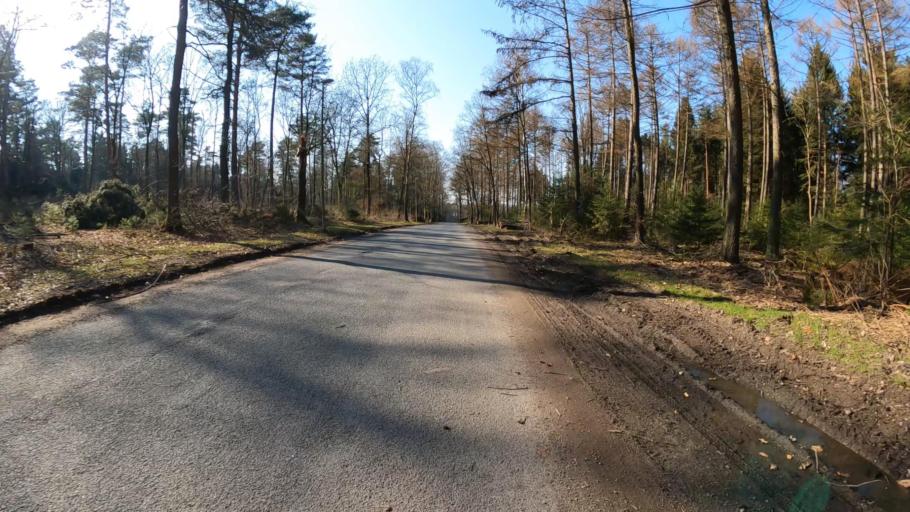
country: DE
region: Lower Saxony
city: Buchholz in der Nordheide
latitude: 53.3093
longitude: 9.8414
